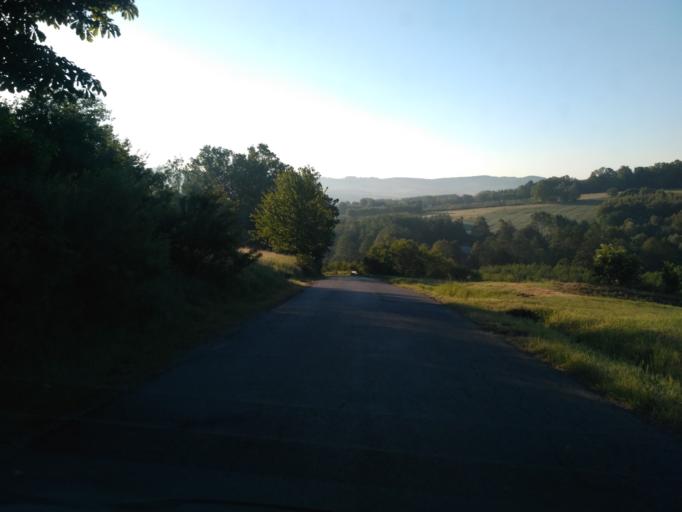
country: PL
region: Subcarpathian Voivodeship
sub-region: Powiat strzyzowski
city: Polomia
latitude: 49.8972
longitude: 21.8699
